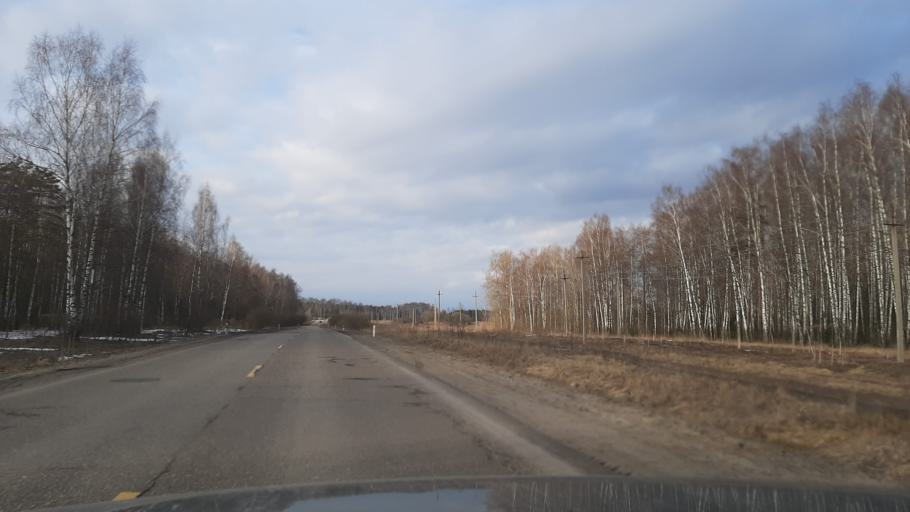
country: RU
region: Ivanovo
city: Novo-Talitsy
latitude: 56.9276
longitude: 40.7364
